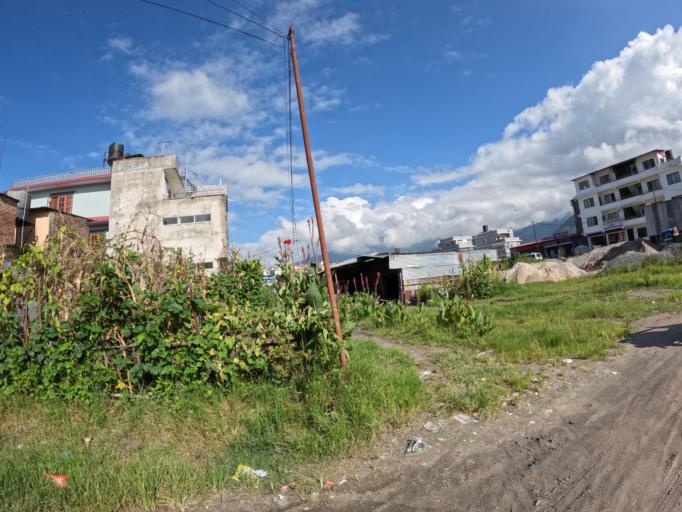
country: NP
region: Central Region
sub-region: Bagmati Zone
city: Kathmandu
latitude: 27.7583
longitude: 85.3357
